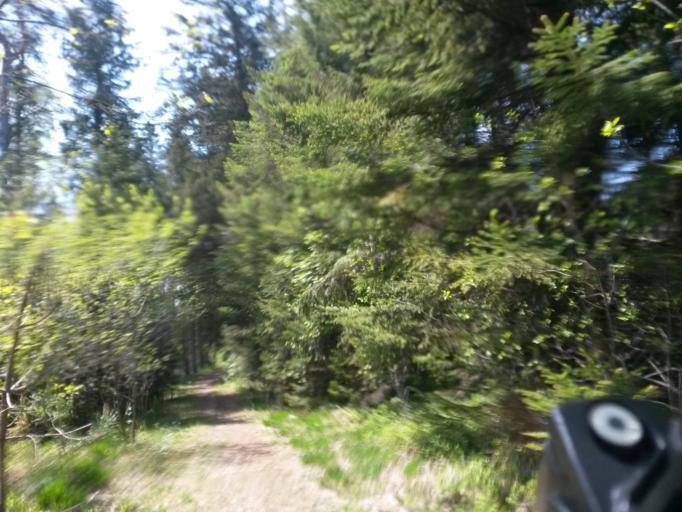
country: DE
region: Baden-Wuerttemberg
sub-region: Tuebingen Region
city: Bad Waldsee
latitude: 47.9240
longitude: 9.7169
